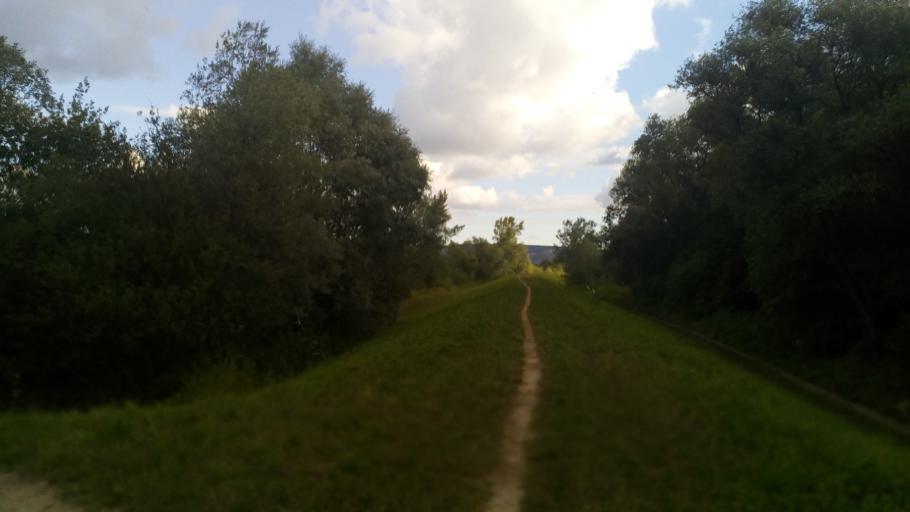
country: PL
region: Lesser Poland Voivodeship
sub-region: Powiat nowosadecki
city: Stary Sacz
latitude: 49.5879
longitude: 20.6542
